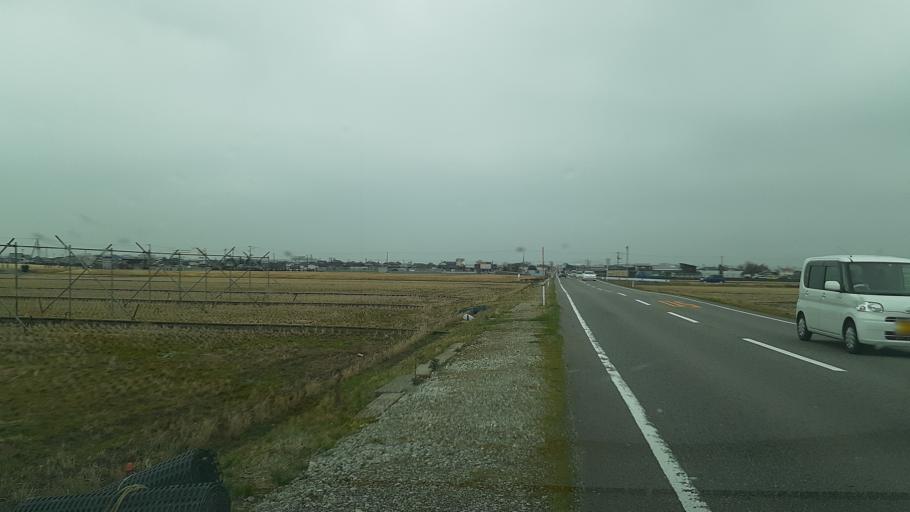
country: JP
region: Niigata
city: Kameda-honcho
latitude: 37.8633
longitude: 139.0702
